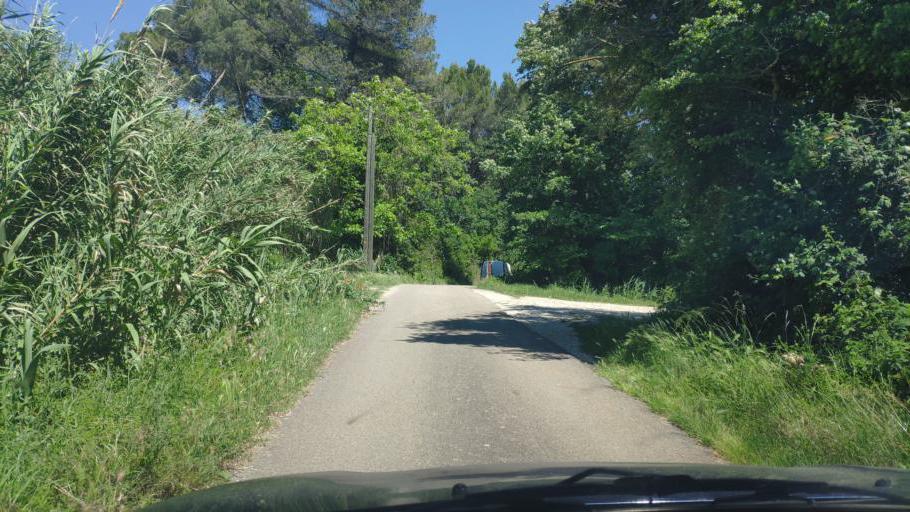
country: FR
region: Provence-Alpes-Cote d'Azur
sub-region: Departement du Vaucluse
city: Aubignan
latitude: 44.0753
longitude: 5.0372
